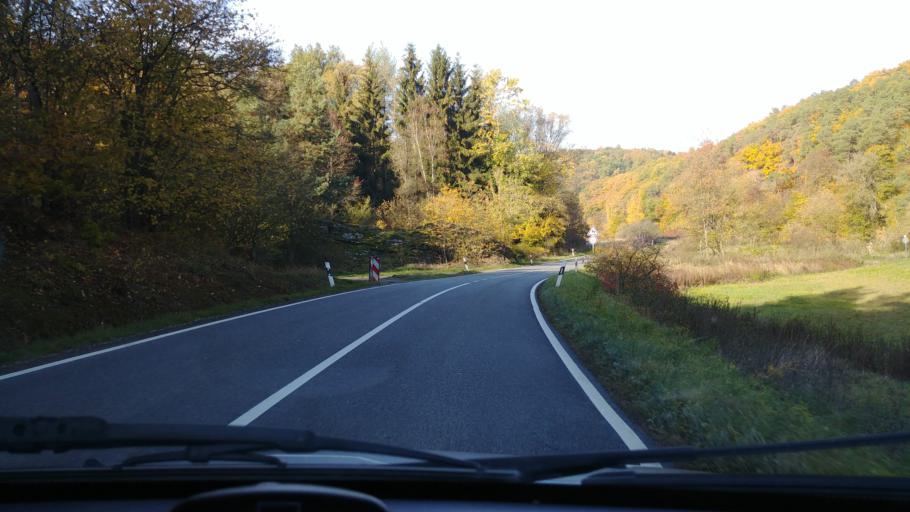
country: DE
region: Hesse
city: Burg Hohenstein
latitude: 50.2170
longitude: 8.0831
